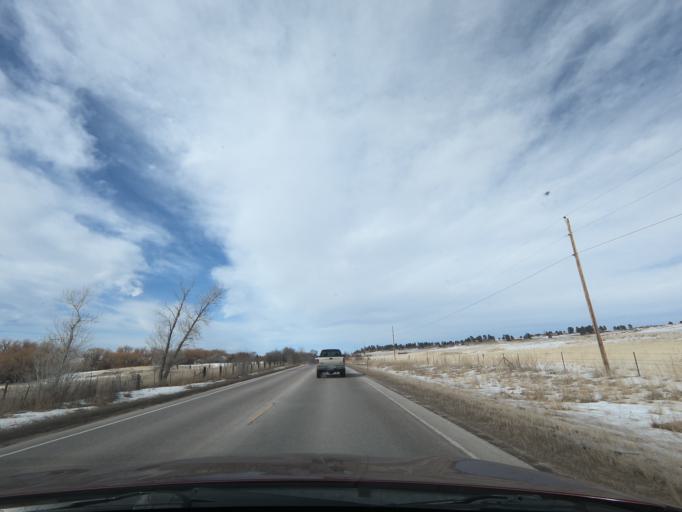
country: US
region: Colorado
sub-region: Elbert County
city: Elizabeth
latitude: 39.2452
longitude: -104.6980
